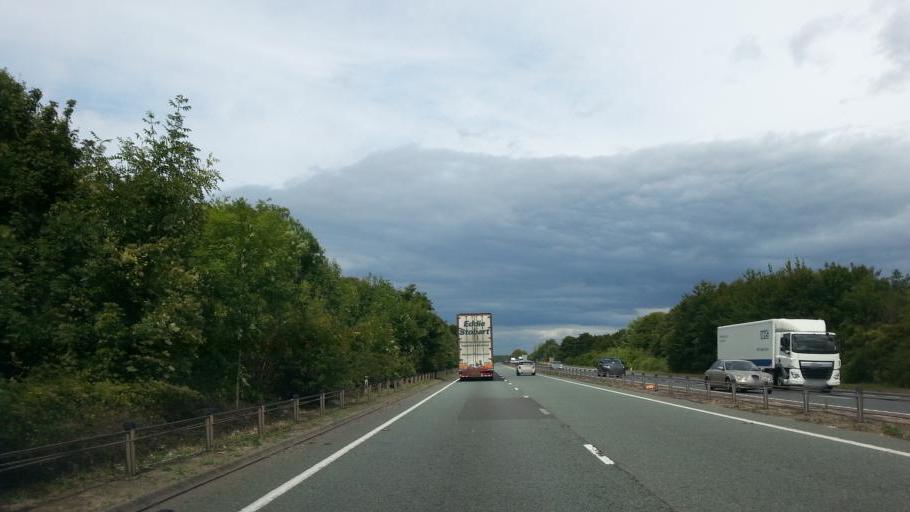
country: GB
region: England
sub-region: Cambridgeshire
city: Sawston
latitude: 52.1000
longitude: 0.2072
